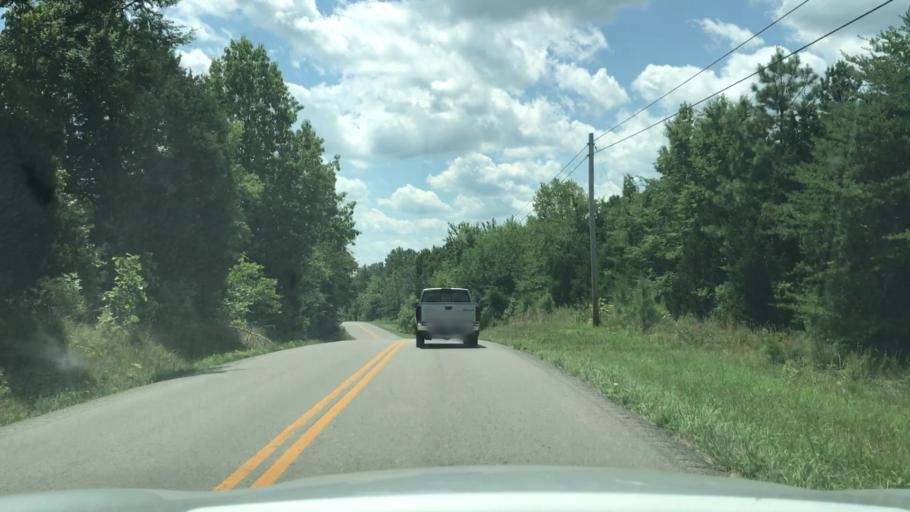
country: US
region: Kentucky
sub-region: Muhlenberg County
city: Greenville
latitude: 37.1776
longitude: -87.2391
